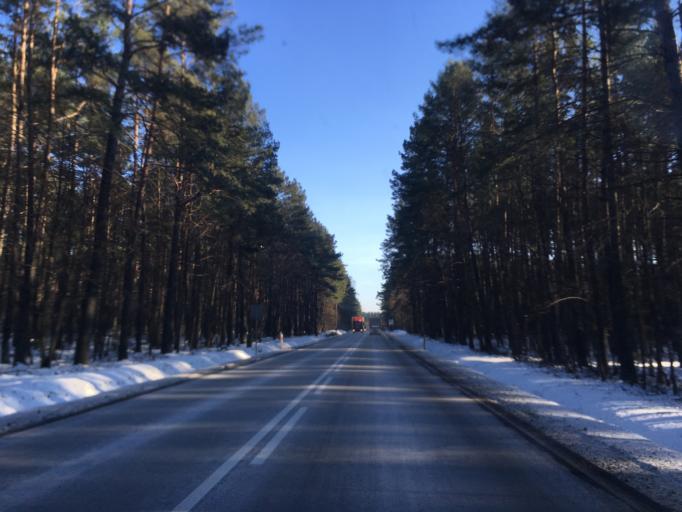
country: PL
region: Pomeranian Voivodeship
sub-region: Powiat koscierski
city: Koscierzyna
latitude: 54.1231
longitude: 17.8817
